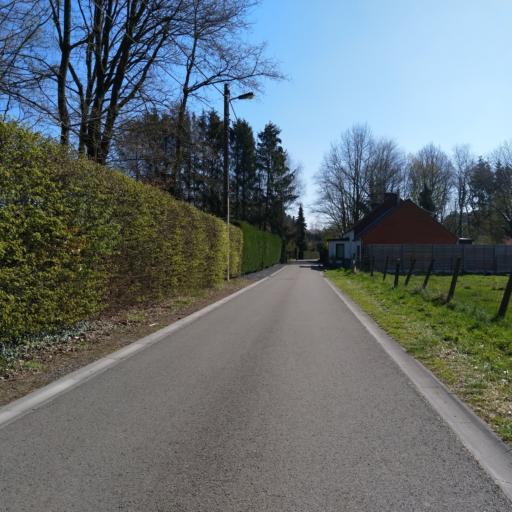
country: BE
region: Wallonia
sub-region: Province du Hainaut
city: Jurbise
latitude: 50.5074
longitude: 3.9344
